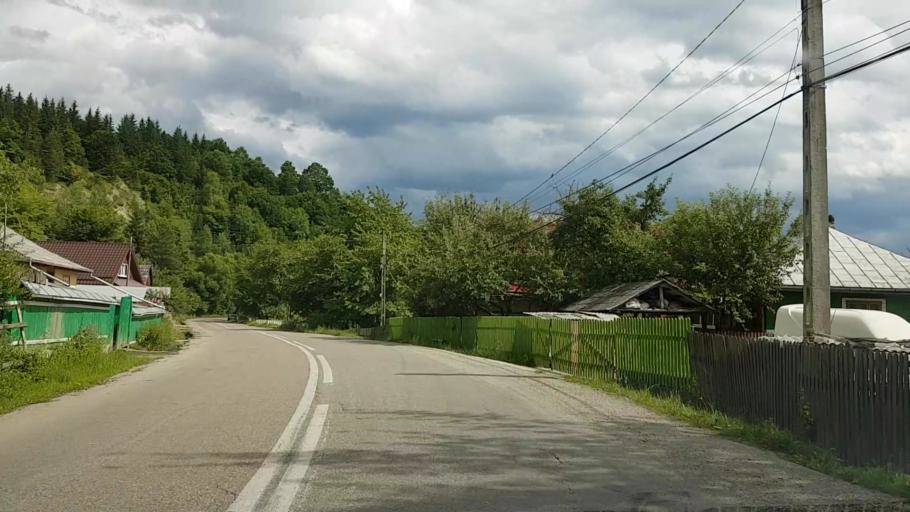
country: RO
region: Neamt
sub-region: Comuna Hangu
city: Hangu
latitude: 47.0294
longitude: 26.0659
